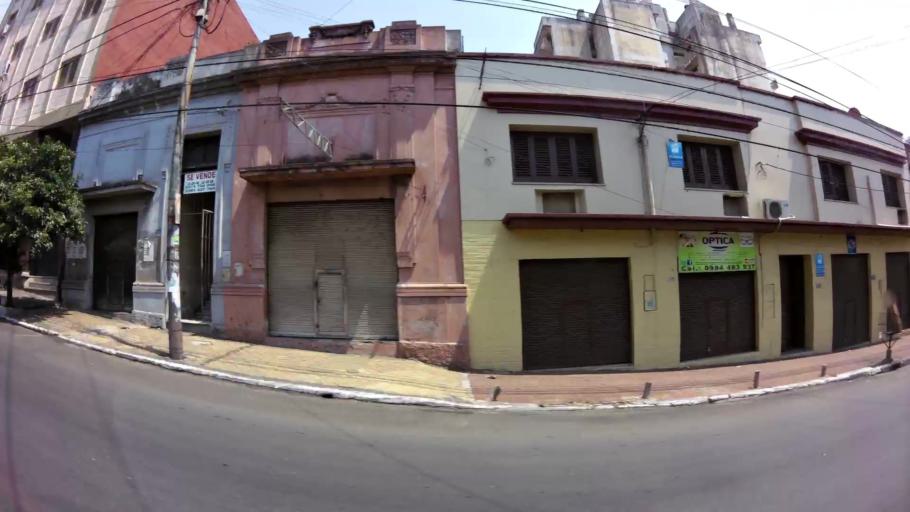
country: PY
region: Asuncion
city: Asuncion
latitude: -25.2814
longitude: -57.6436
